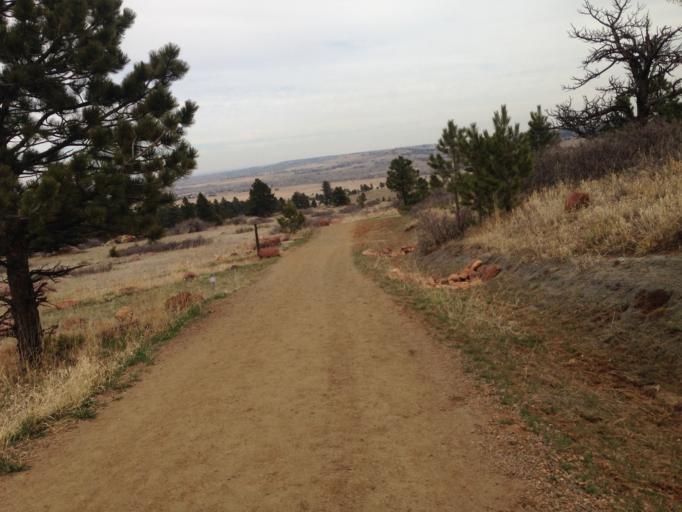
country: US
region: Colorado
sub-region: Boulder County
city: Boulder
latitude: 39.9472
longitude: -105.2664
